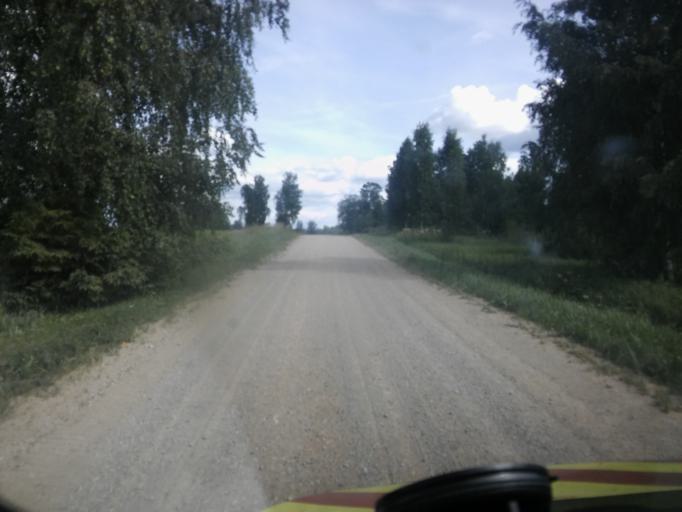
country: EE
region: Viljandimaa
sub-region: Karksi vald
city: Karksi-Nuia
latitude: 58.0839
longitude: 25.5081
